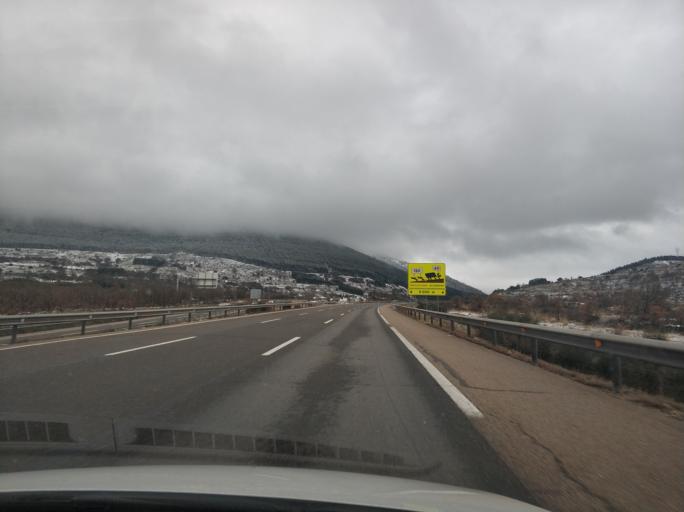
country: ES
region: Castille and Leon
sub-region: Provincia de Segovia
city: Cerezo de Abajo
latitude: 41.1802
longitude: -3.5838
